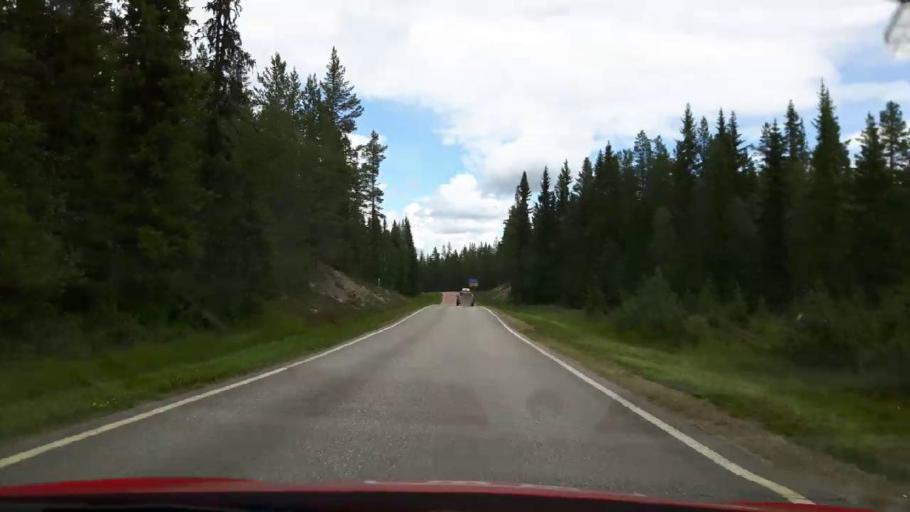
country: NO
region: Hedmark
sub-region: Trysil
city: Innbygda
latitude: 61.8613
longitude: 12.9491
